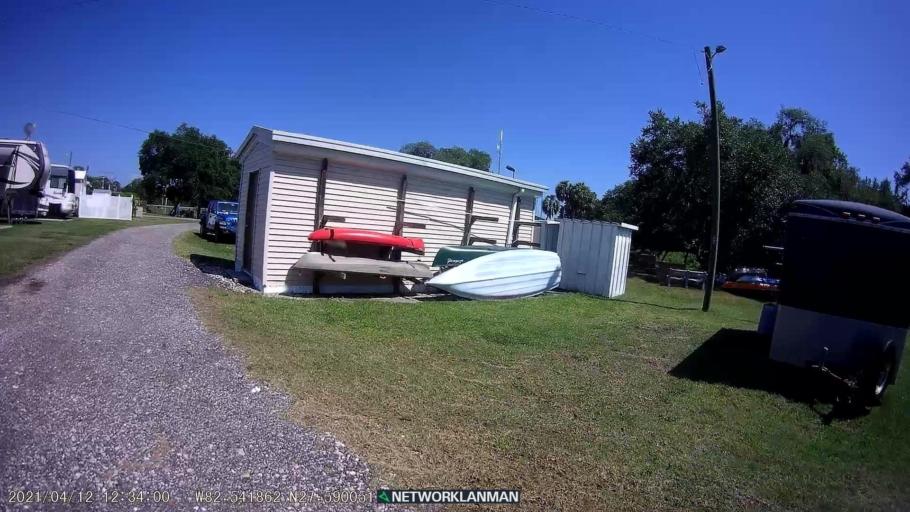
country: US
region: Florida
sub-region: Manatee County
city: Memphis
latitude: 27.5910
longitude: -82.5431
